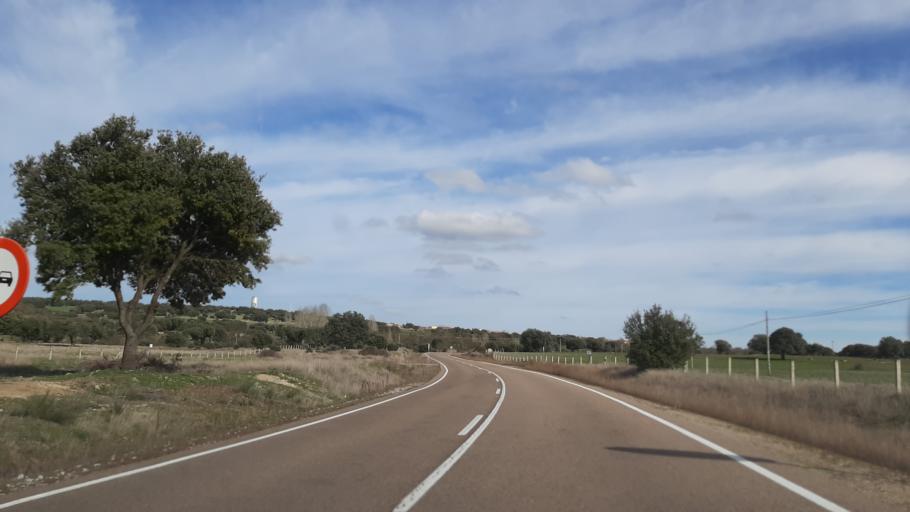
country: ES
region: Castille and Leon
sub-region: Provincia de Salamanca
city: Monleras
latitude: 41.1862
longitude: -6.2396
